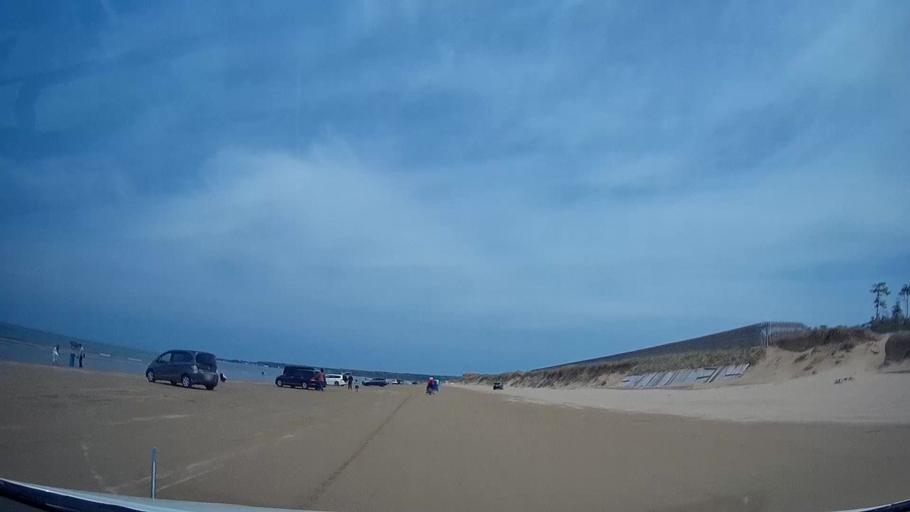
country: JP
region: Ishikawa
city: Hakui
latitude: 36.8870
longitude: 136.7642
